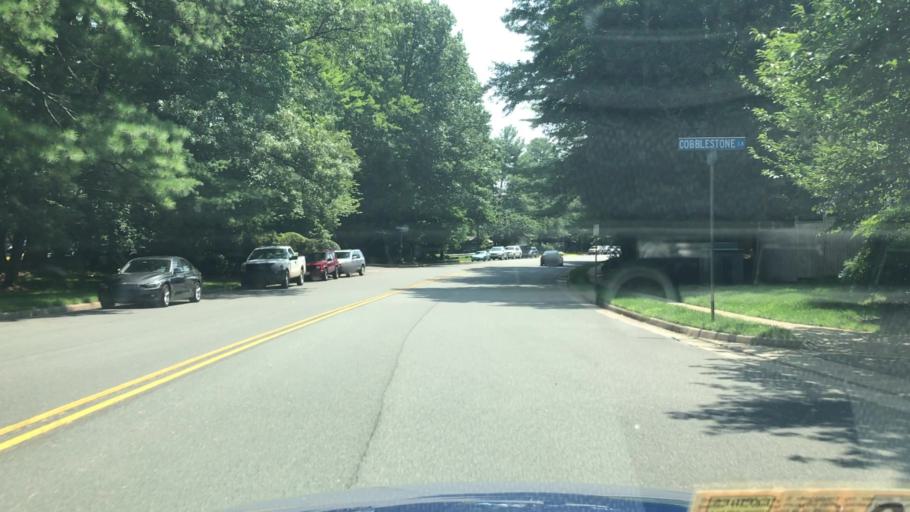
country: US
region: Virginia
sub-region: Fairfax County
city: Reston
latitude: 38.9360
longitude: -77.3365
